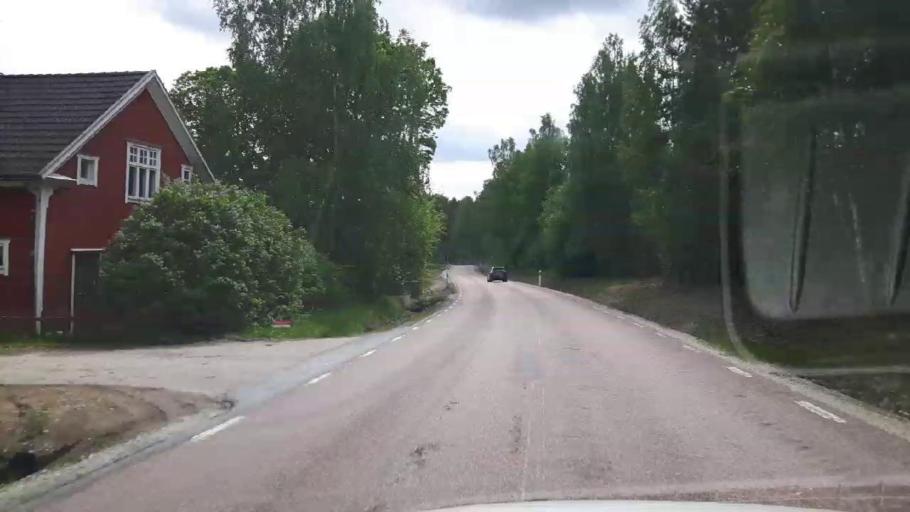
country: SE
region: Vaestmanland
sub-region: Skinnskattebergs Kommun
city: Skinnskatteberg
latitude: 59.8580
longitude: 15.8419
